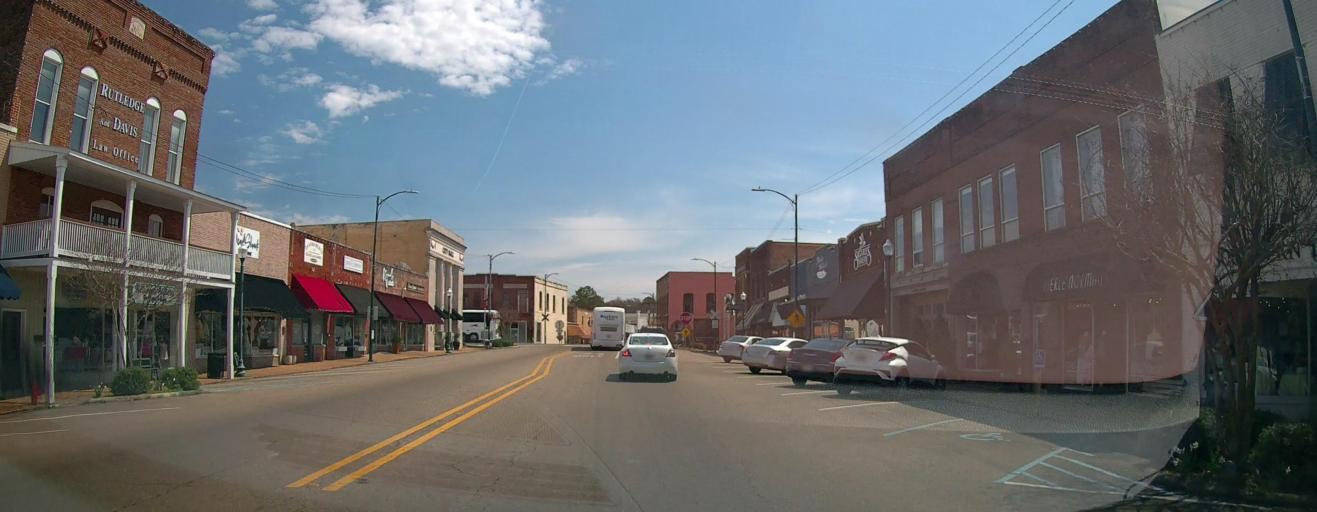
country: US
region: Mississippi
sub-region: Union County
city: New Albany
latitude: 34.4942
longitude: -89.0091
